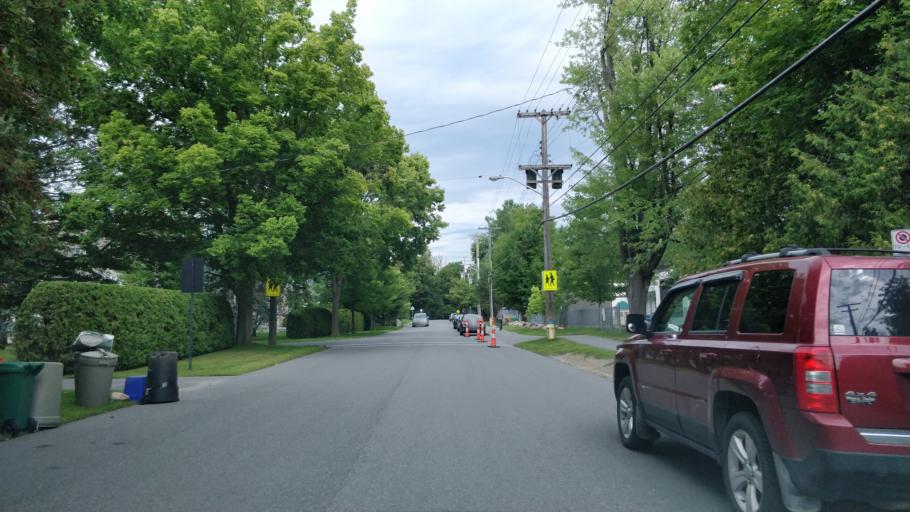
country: CA
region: Quebec
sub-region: Outaouais
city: Gatineau
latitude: 45.4494
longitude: -75.6787
